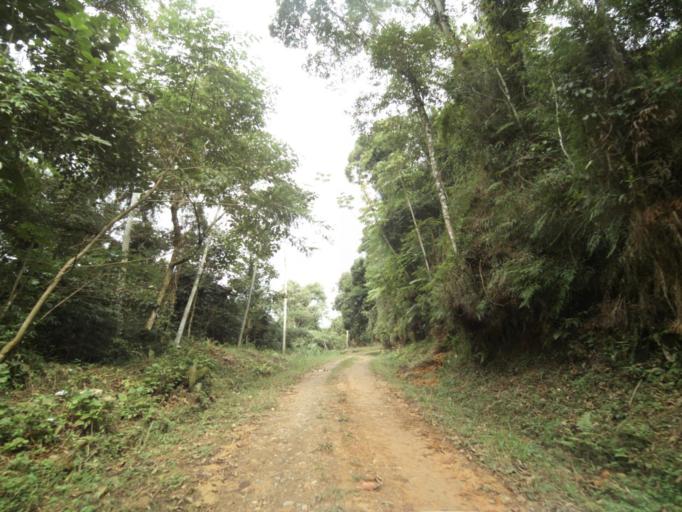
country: BR
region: Santa Catarina
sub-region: Pomerode
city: Pomerode
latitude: -26.7406
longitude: -49.1873
